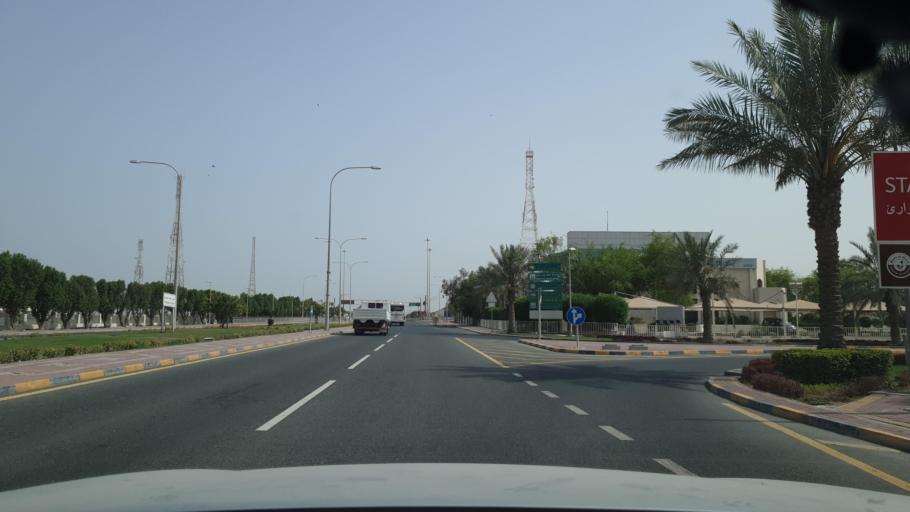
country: QA
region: Al Wakrah
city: Umm Sa'id
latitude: 24.9932
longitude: 51.5488
